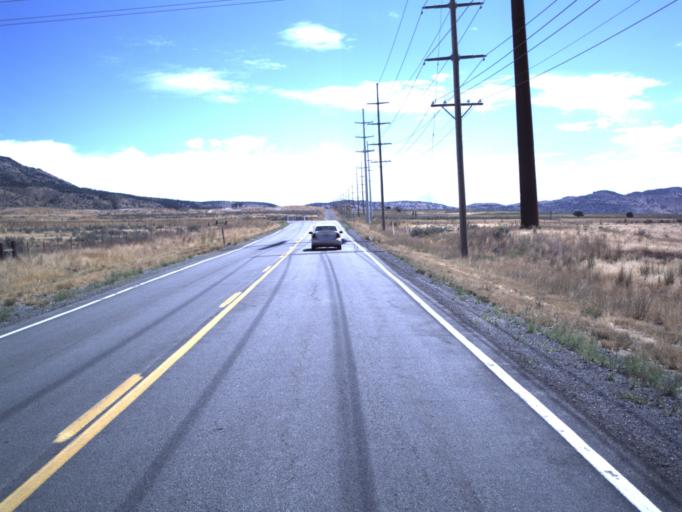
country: US
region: Utah
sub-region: Box Elder County
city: Garland
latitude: 41.8865
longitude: -112.1630
